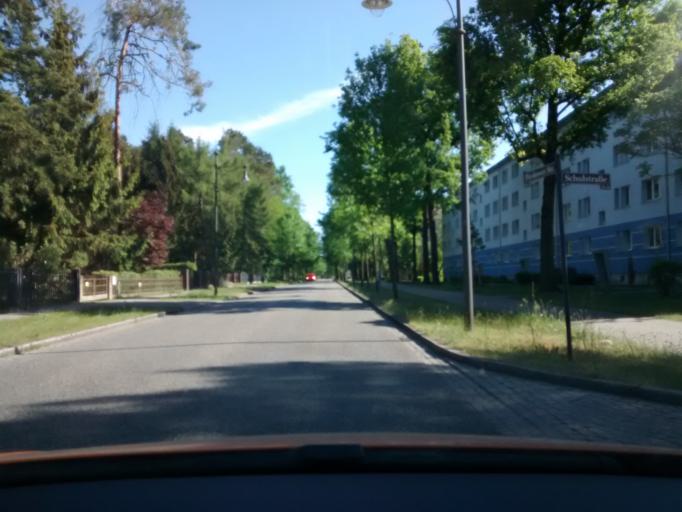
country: DE
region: Brandenburg
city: Bad Saarow
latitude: 52.2891
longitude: 14.0637
